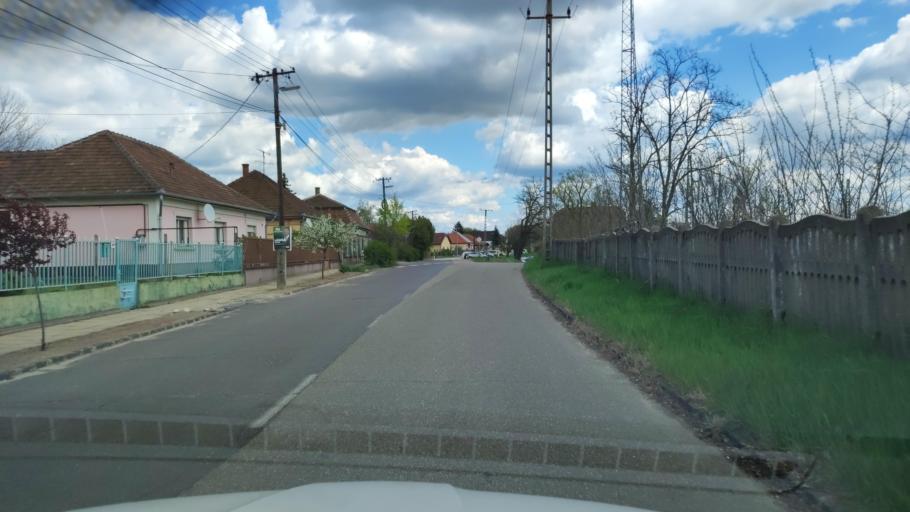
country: HU
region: Pest
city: Cegledbercel
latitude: 47.2115
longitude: 19.6843
